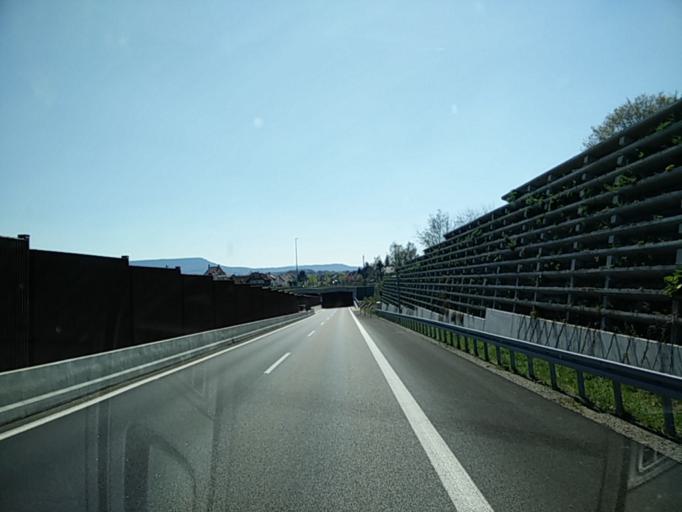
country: DE
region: Baden-Wuerttemberg
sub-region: Tuebingen Region
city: Dusslingen
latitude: 48.4527
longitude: 9.0612
